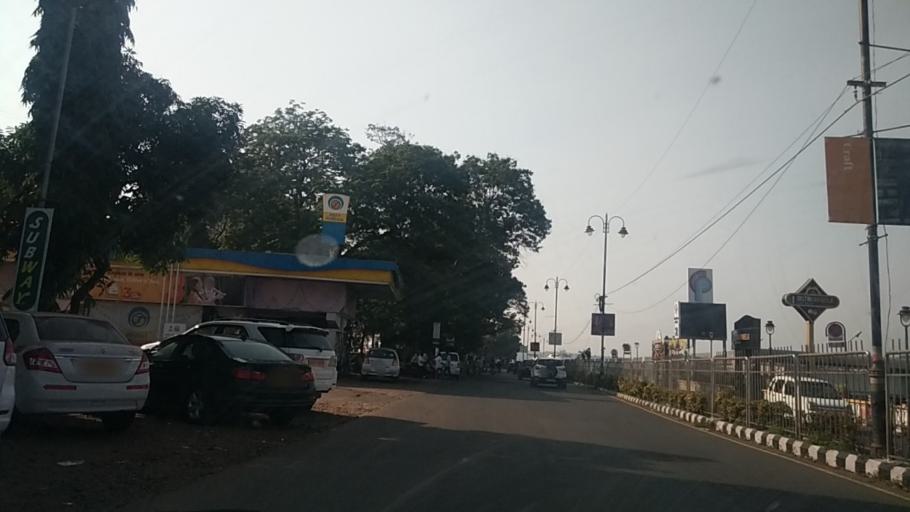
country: IN
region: Goa
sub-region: North Goa
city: Panaji
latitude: 15.5001
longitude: 73.8321
